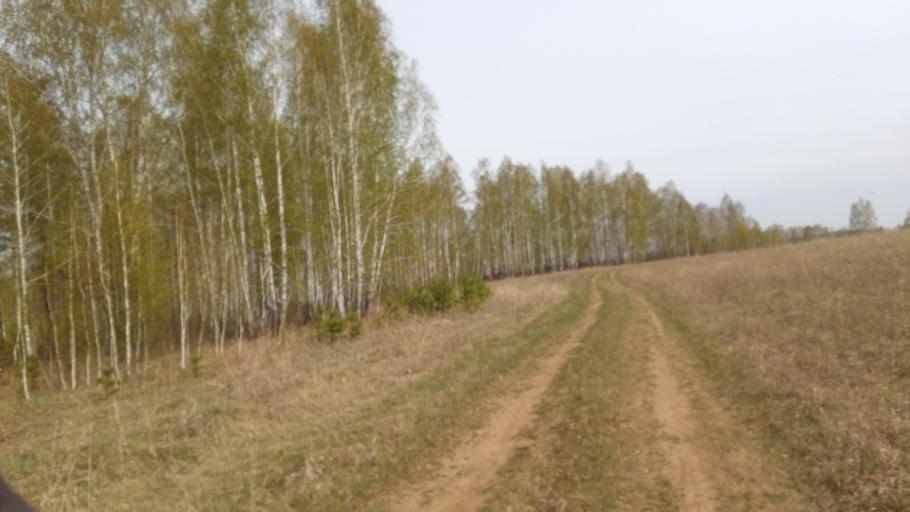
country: RU
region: Chelyabinsk
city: Timiryazevskiy
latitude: 55.0220
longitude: 60.8588
